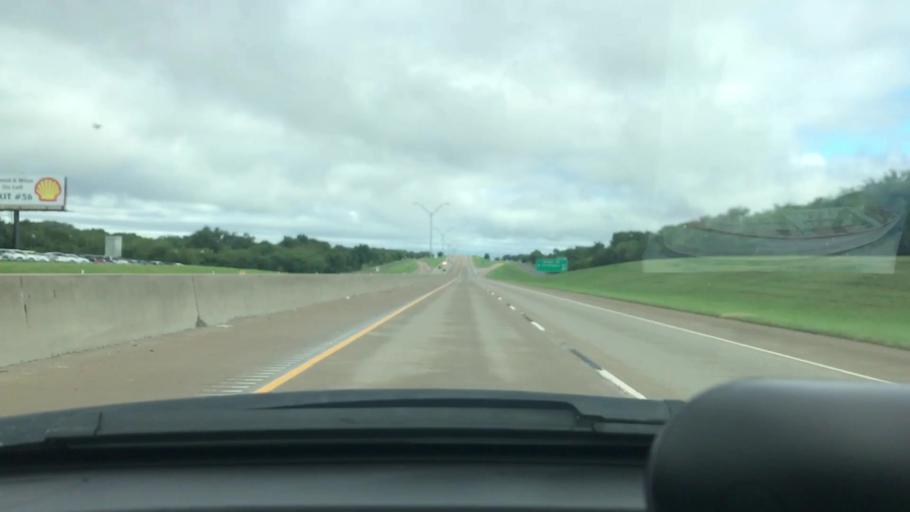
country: US
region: Texas
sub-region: Grayson County
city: Van Alstyne
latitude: 33.4557
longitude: -96.6075
